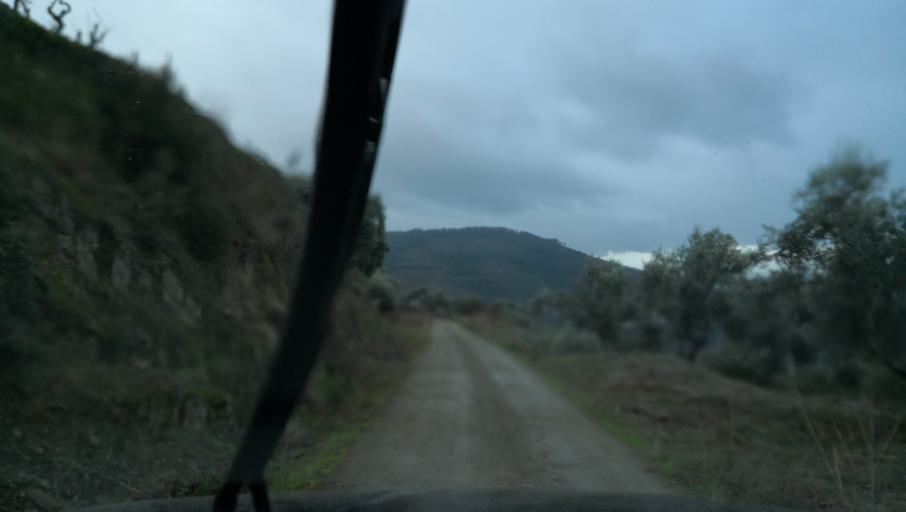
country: PT
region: Vila Real
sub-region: Vila Real
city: Vila Real
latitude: 41.2413
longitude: -7.7485
